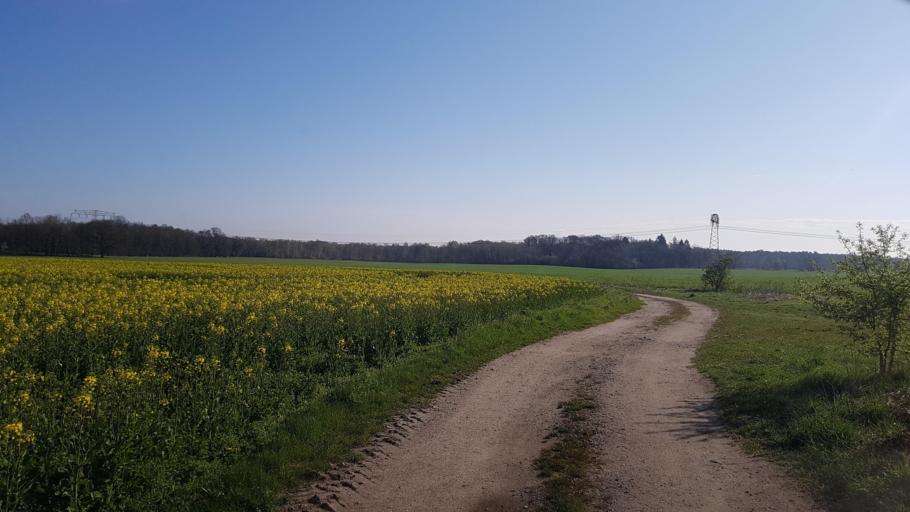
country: DE
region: Brandenburg
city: Altdobern
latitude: 51.6671
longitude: 13.9965
